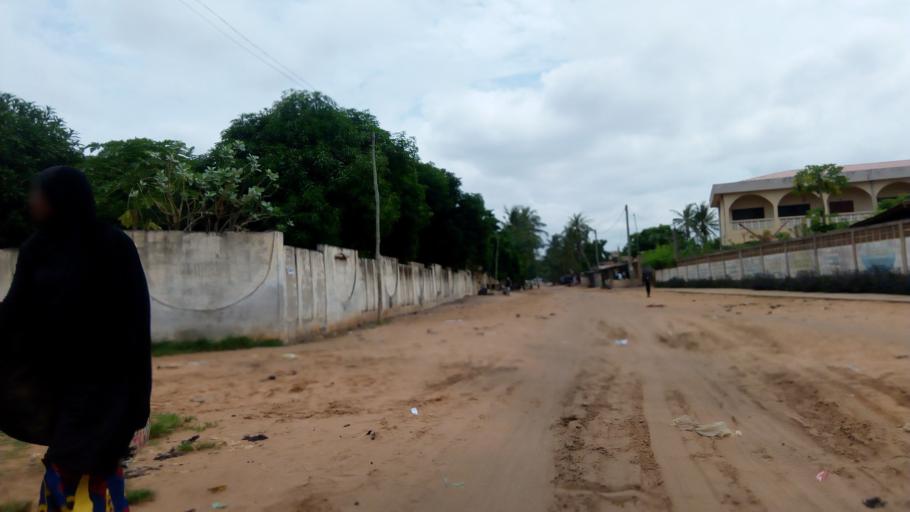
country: TG
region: Maritime
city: Lome
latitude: 6.1659
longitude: 1.2078
